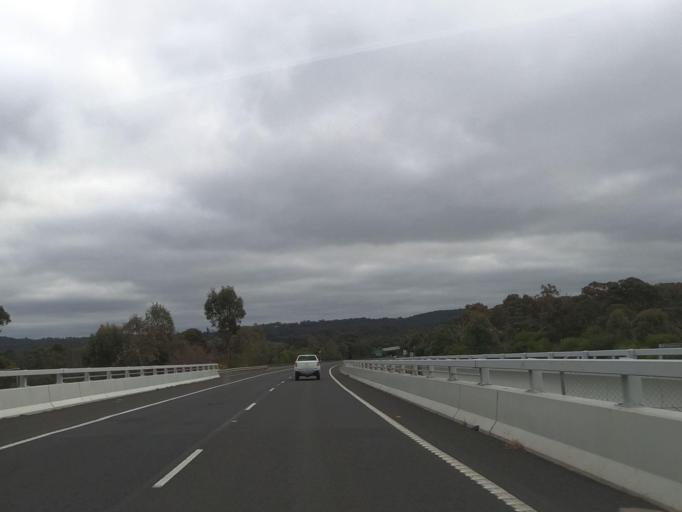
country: AU
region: Victoria
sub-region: Mount Alexander
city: Castlemaine
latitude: -37.0134
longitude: 144.2549
